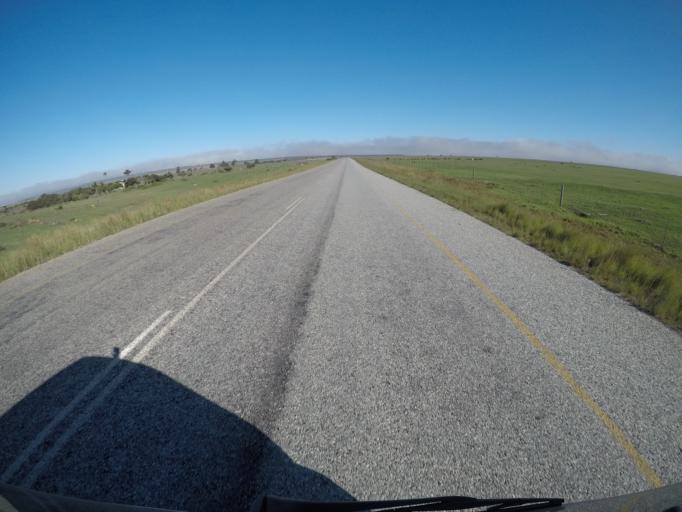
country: ZA
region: Western Cape
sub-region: Eden District Municipality
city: Mossel Bay
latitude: -34.1706
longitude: 22.0137
